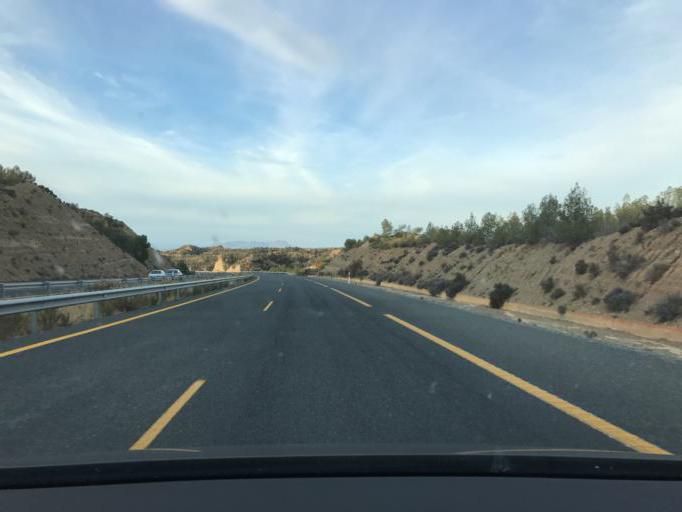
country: ES
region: Andalusia
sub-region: Provincia de Granada
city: Guadix
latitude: 37.2774
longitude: -3.0958
